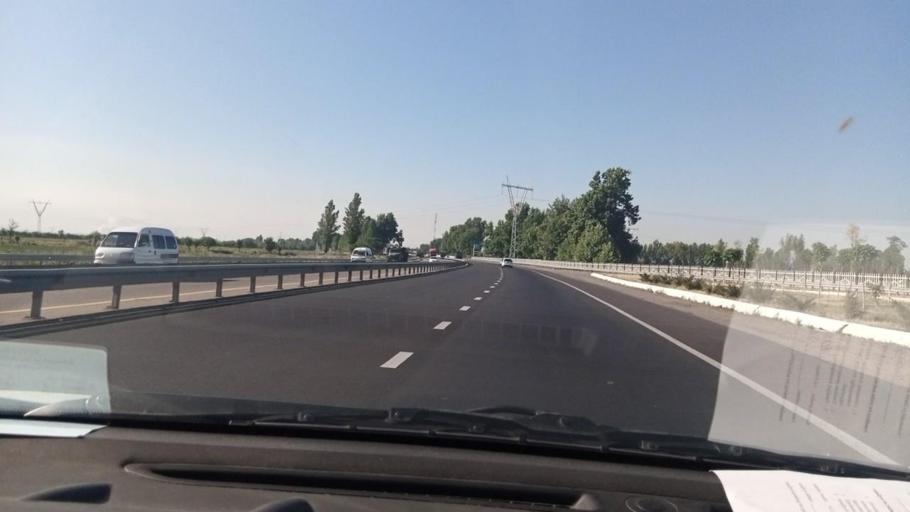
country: UZ
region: Toshkent Shahri
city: Bektemir
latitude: 41.1895
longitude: 69.4032
